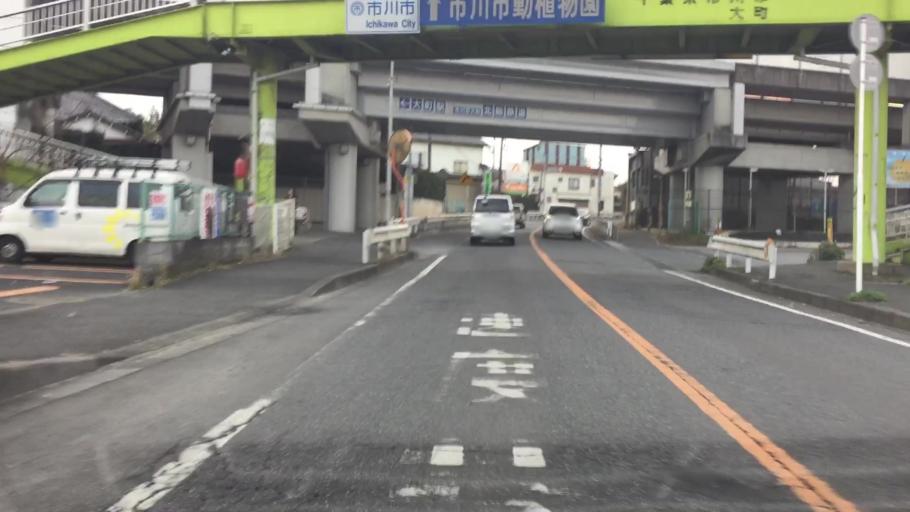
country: JP
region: Chiba
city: Matsudo
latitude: 35.7755
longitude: 139.9731
